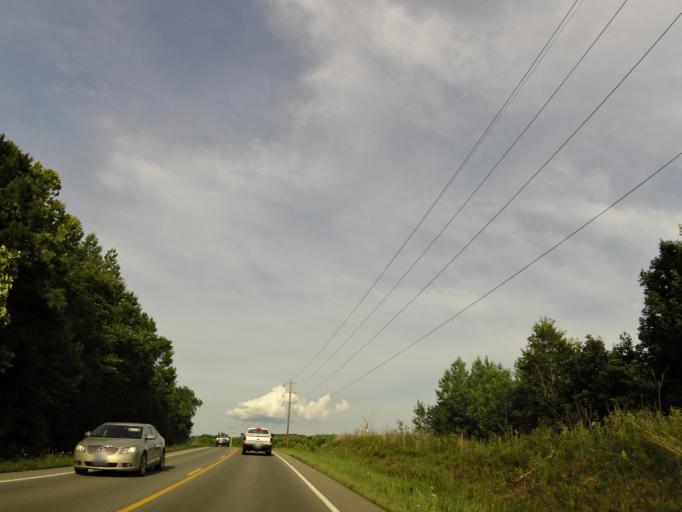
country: US
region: Tennessee
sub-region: Humphreys County
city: McEwen
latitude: 36.0928
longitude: -87.5531
